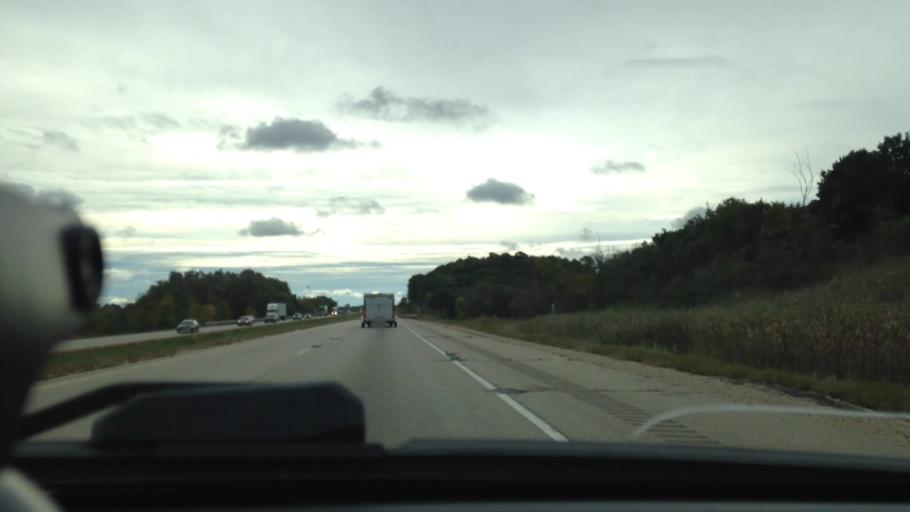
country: US
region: Wisconsin
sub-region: Dodge County
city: Theresa
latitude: 43.5231
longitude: -88.3862
